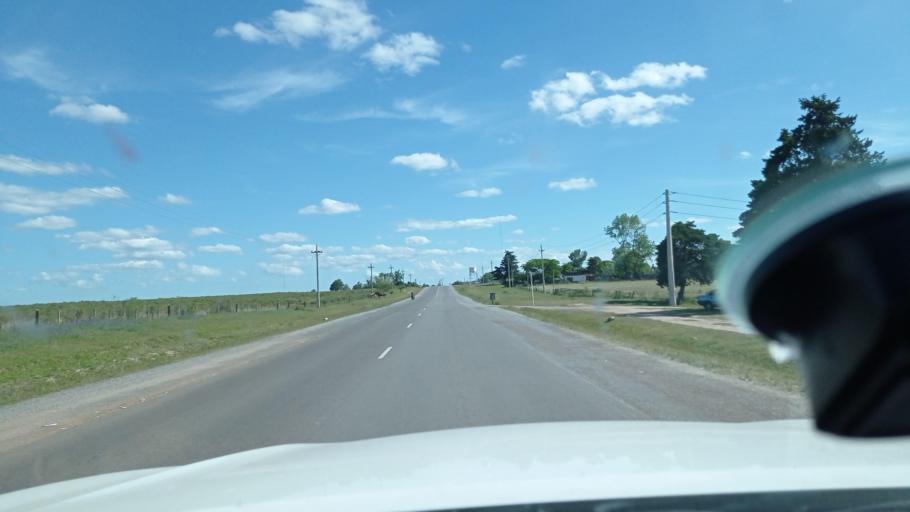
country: UY
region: Florida
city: Florida
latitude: -34.0813
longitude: -56.2358
